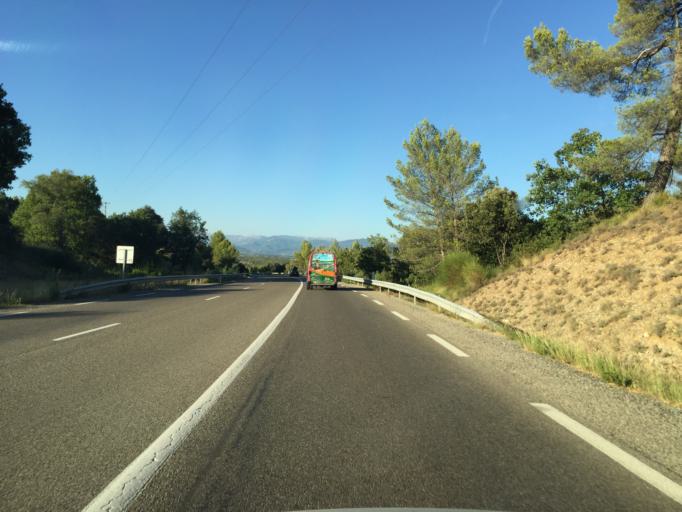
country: FR
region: Provence-Alpes-Cote d'Azur
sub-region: Departement des Alpes-de-Haute-Provence
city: Oraison
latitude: 43.9611
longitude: 5.8999
